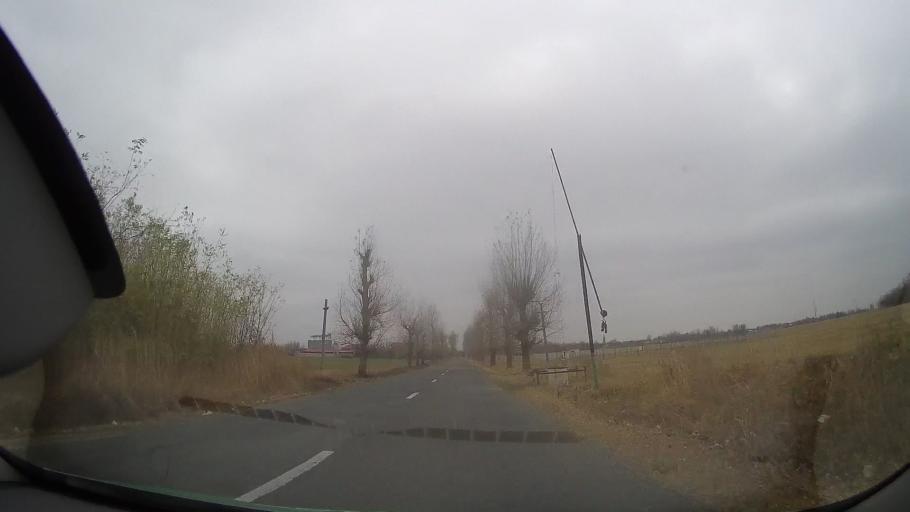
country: RO
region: Ialomita
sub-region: Comuna Grindu
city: Grindu
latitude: 44.7848
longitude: 26.9038
